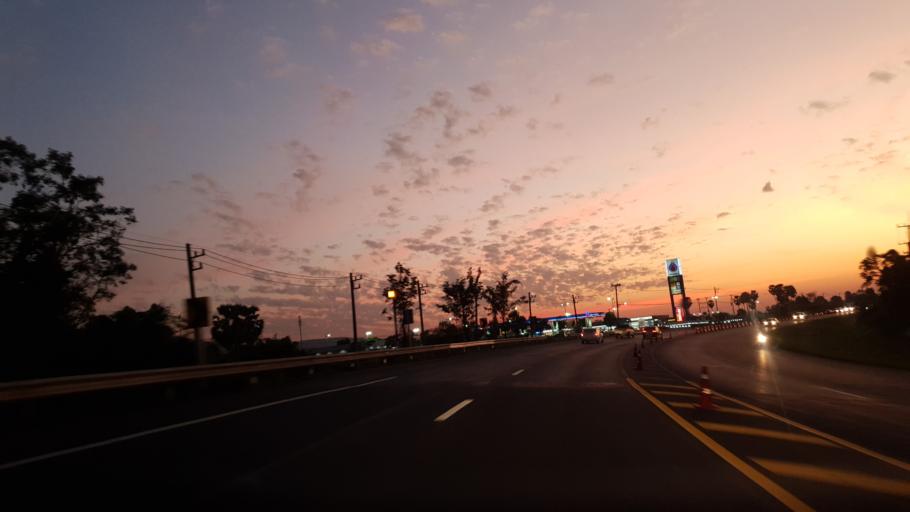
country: TH
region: Phitsanulok
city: Wang Thong
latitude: 16.8562
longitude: 100.4800
